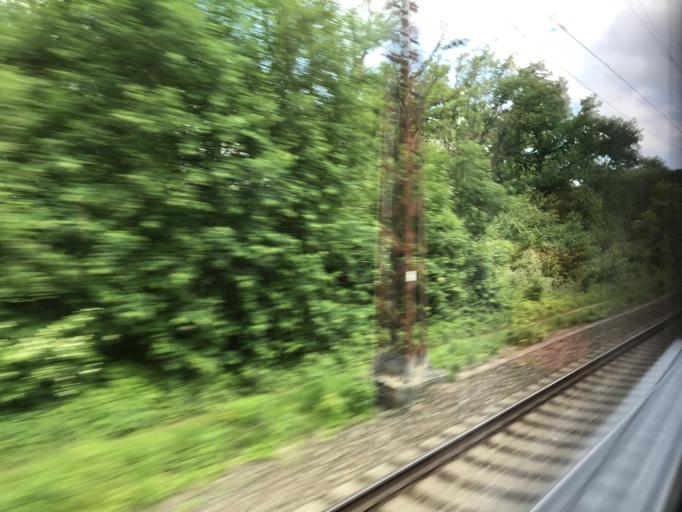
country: DE
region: Bavaria
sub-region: Swabia
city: Rettenbach
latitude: 48.4783
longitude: 10.3360
